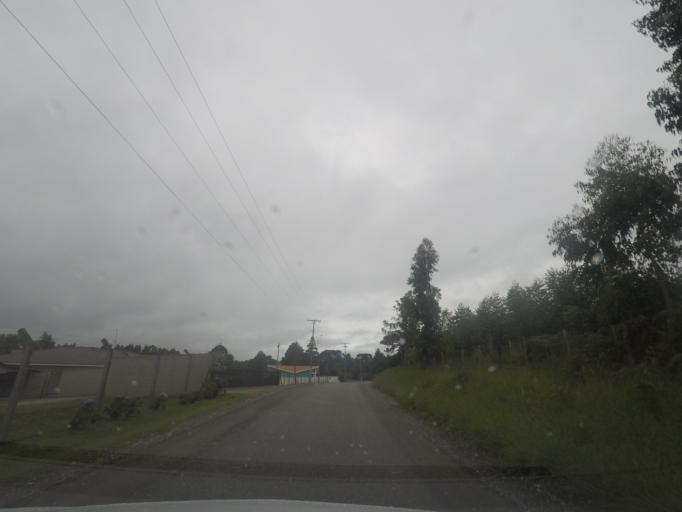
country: BR
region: Parana
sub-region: Campina Grande Do Sul
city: Campina Grande do Sul
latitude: -25.3107
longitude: -49.0904
